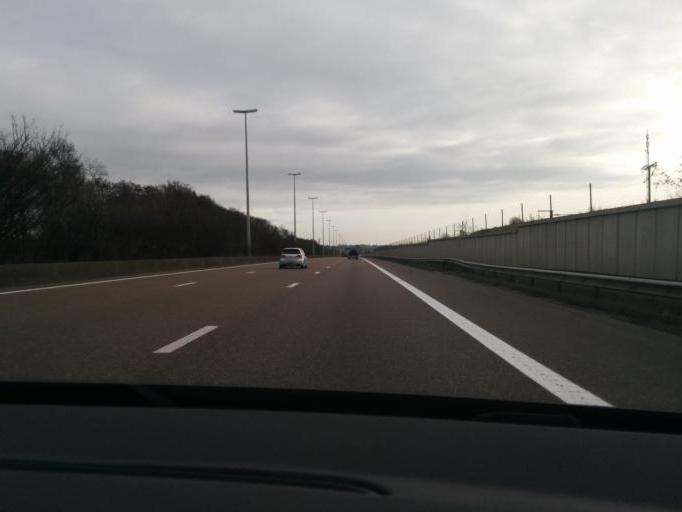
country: BE
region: Flanders
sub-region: Provincie Vlaams-Brabant
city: Hoegaarden
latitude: 50.7936
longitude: 4.8978
